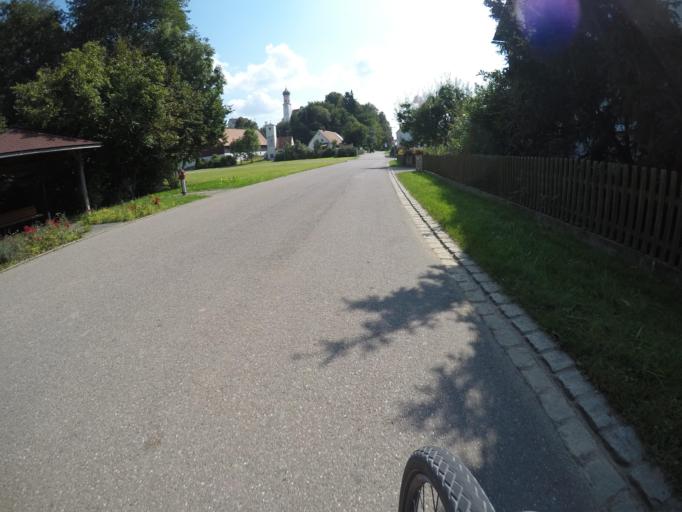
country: DE
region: Bavaria
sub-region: Swabia
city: Laugna
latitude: 48.5425
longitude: 10.7376
